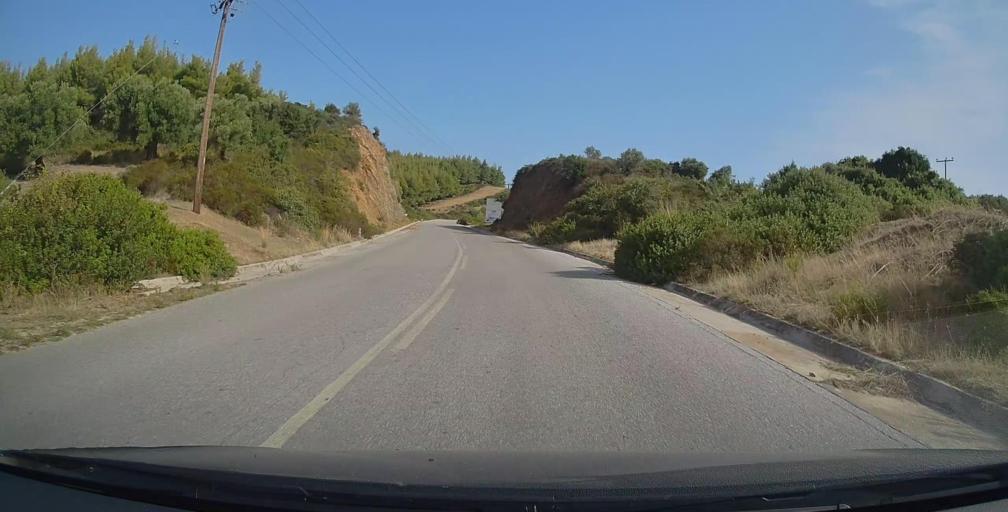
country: GR
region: Central Macedonia
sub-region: Nomos Chalkidikis
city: Sykia
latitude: 39.9631
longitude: 23.9482
